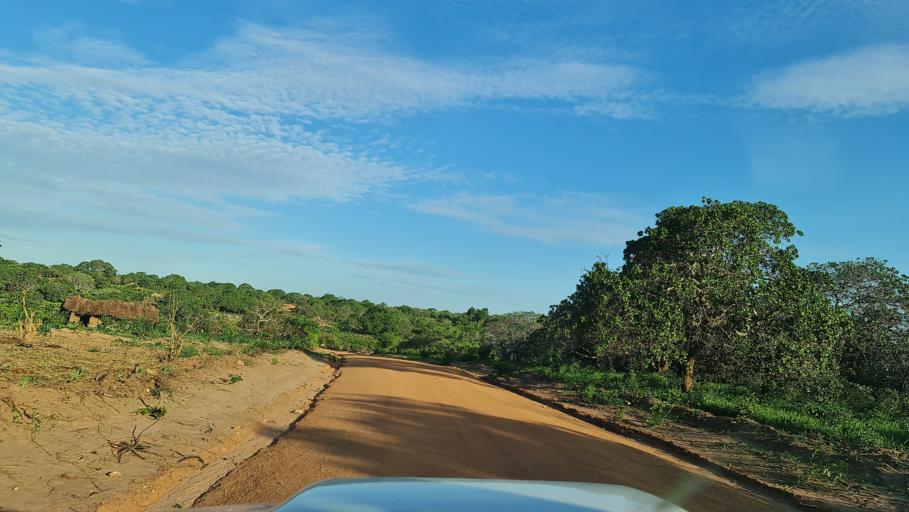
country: MZ
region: Nampula
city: Nacala
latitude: -14.6727
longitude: 40.2804
